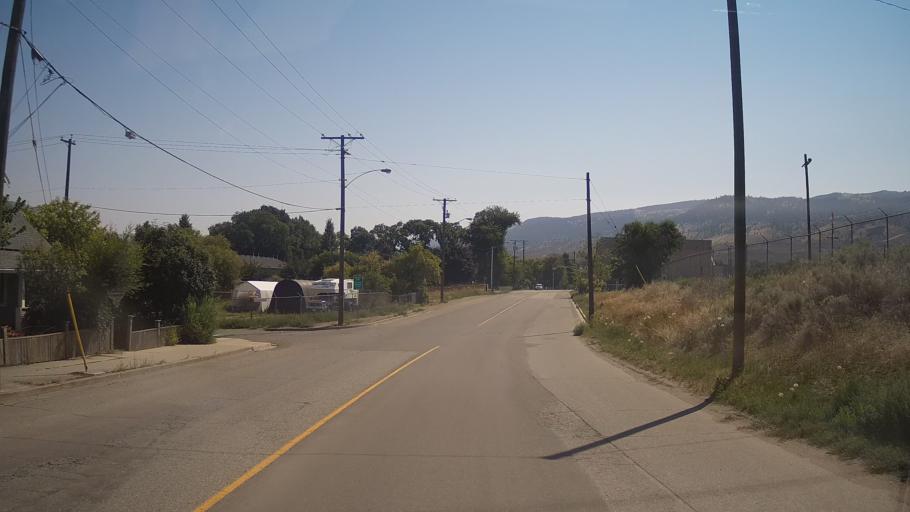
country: CA
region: British Columbia
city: Kamloops
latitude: 50.6780
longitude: -120.3236
